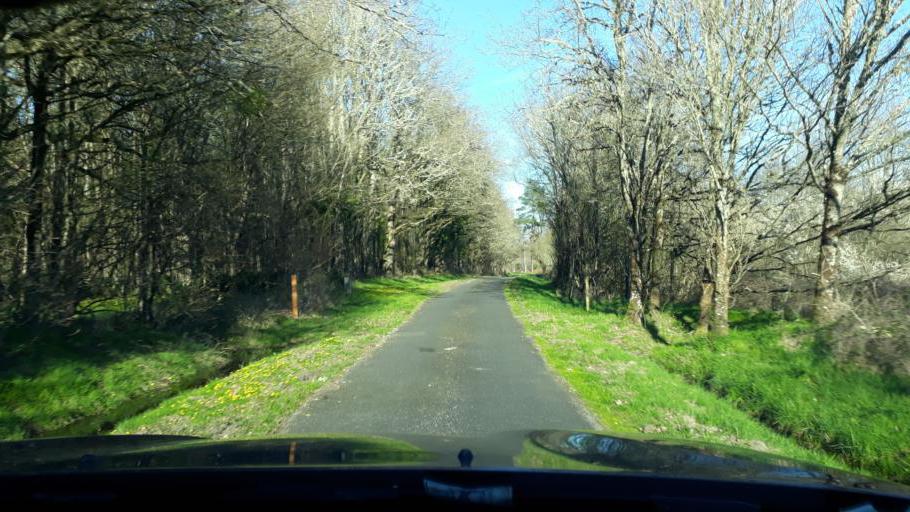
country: FR
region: Centre
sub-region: Departement du Loiret
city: Ligny-le-Ribault
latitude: 47.7016
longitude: 1.8138
